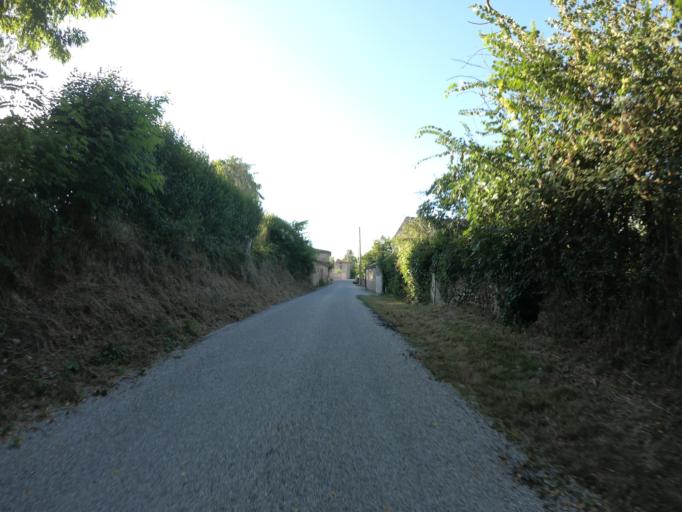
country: FR
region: Midi-Pyrenees
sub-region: Departement de l'Ariege
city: La Tour-du-Crieu
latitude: 43.1095
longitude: 1.7256
